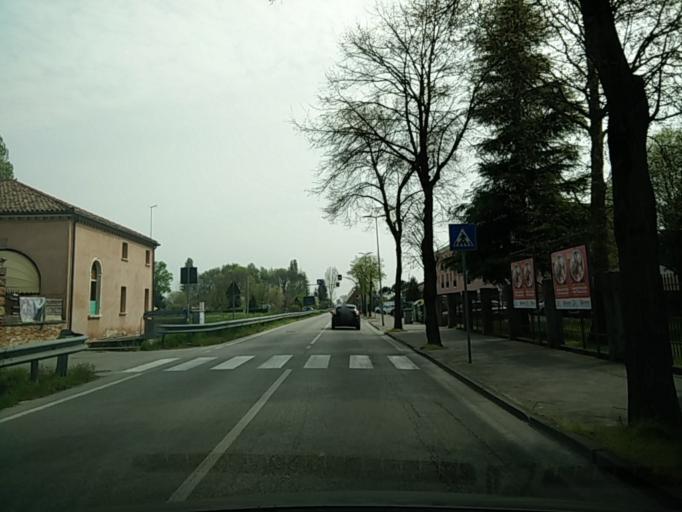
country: IT
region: Veneto
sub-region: Provincia di Venezia
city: Caltana
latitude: 45.4789
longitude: 12.0314
